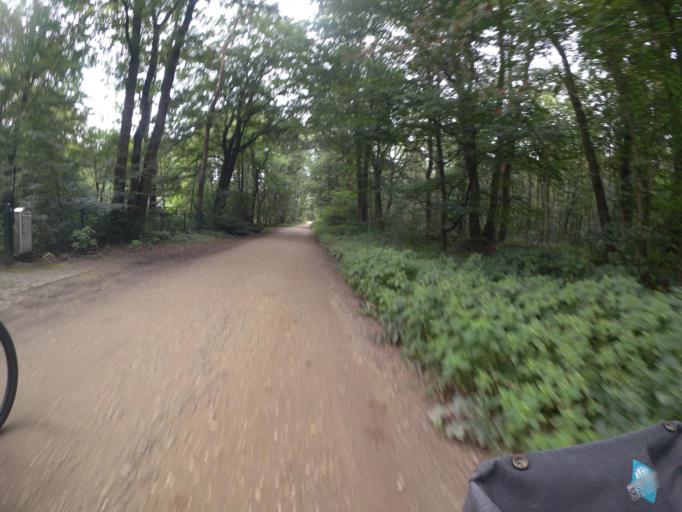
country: NL
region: Gelderland
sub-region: Gemeente Groesbeek
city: Bredeweg
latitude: 51.7591
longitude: 5.9134
